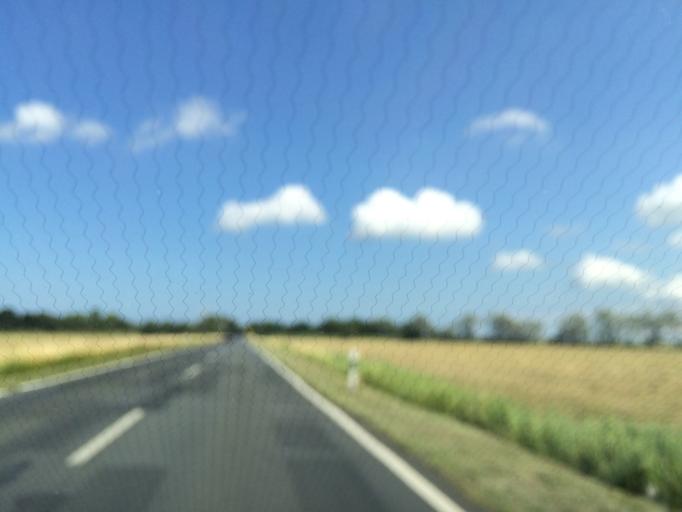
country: DE
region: Mecklenburg-Vorpommern
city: Zingst
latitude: 54.4229
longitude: 12.6669
